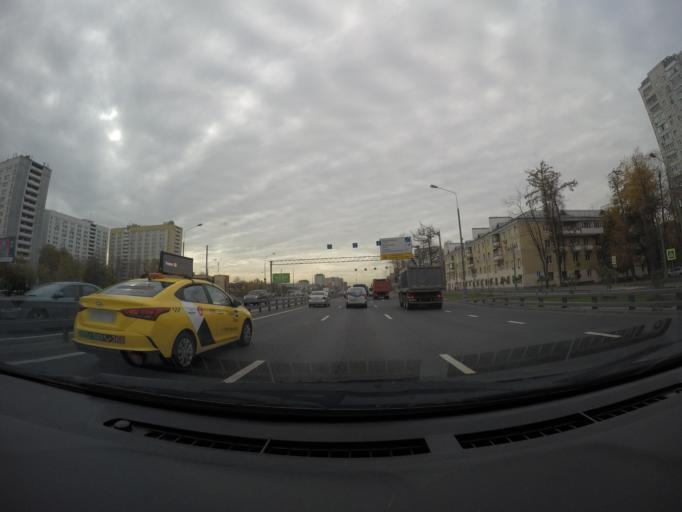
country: RU
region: Moscow
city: Yaroslavskiy
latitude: 55.8684
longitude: 37.7081
